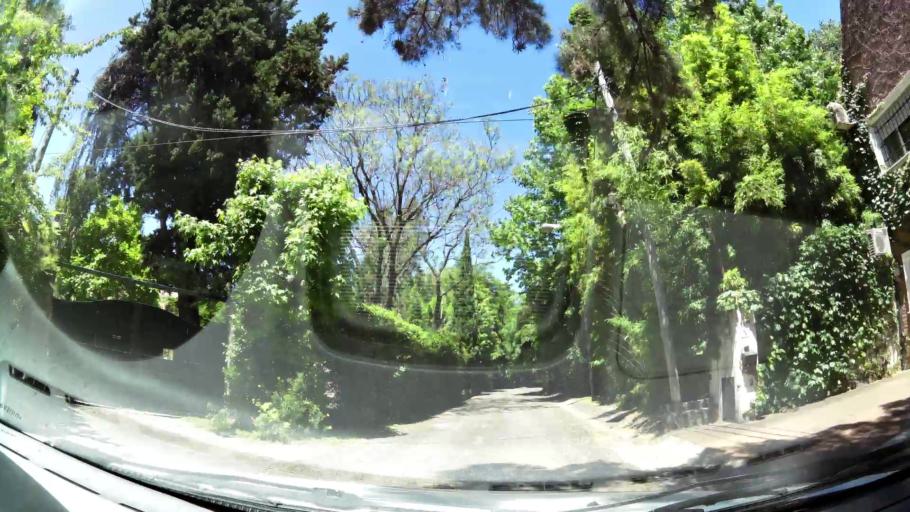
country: AR
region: Buenos Aires
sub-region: Partido de Tigre
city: Tigre
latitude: -34.4919
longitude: -58.5725
